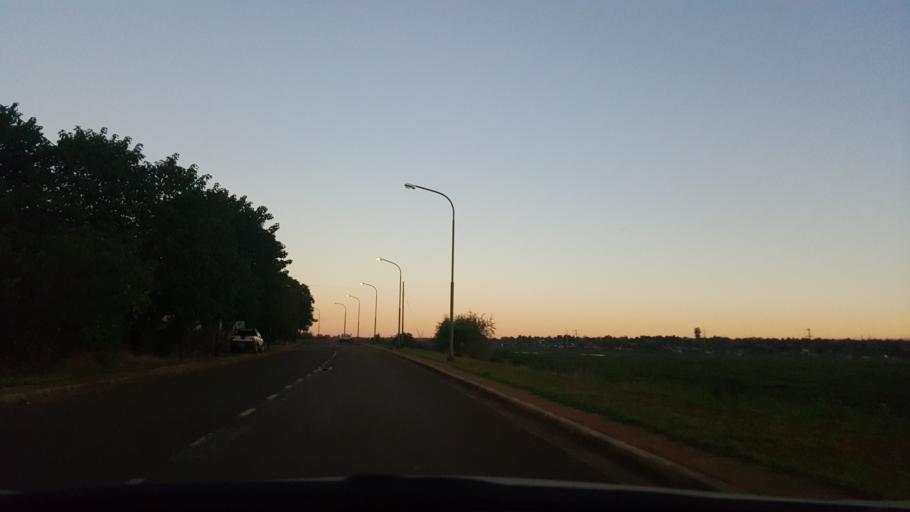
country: AR
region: Misiones
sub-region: Departamento de Capital
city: Posadas
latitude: -27.4224
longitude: -55.9047
